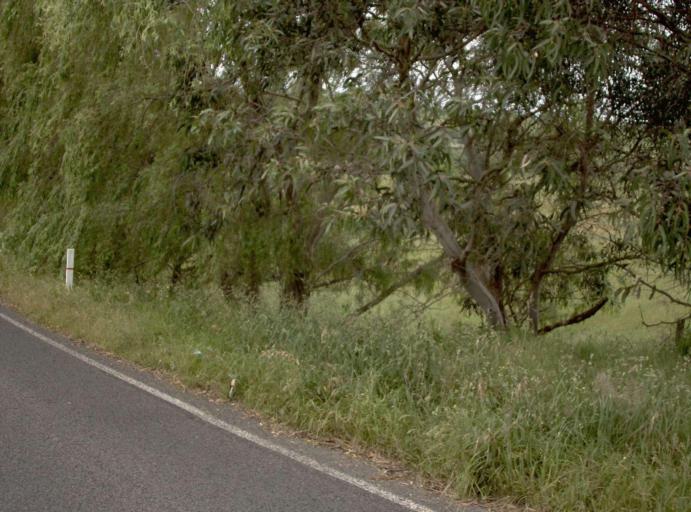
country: AU
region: Victoria
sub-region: Bass Coast
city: North Wonthaggi
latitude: -38.5124
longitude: 145.7178
